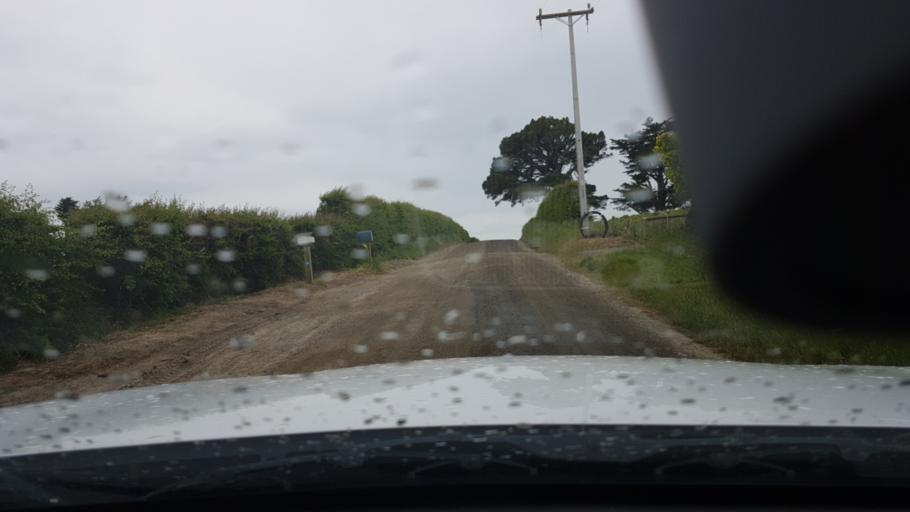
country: NZ
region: Otago
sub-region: Dunedin City
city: Dunedin
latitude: -45.9174
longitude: 170.4305
